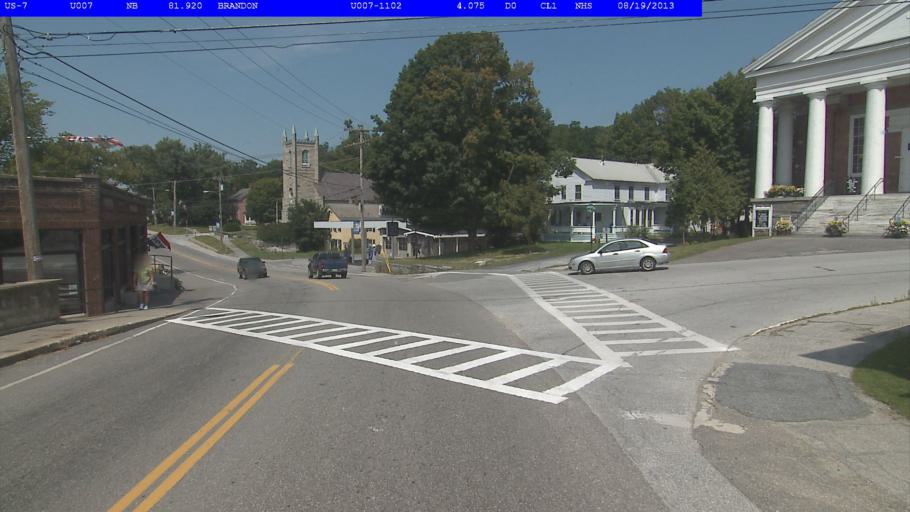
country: US
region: Vermont
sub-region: Rutland County
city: Brandon
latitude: 43.7996
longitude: -73.0891
